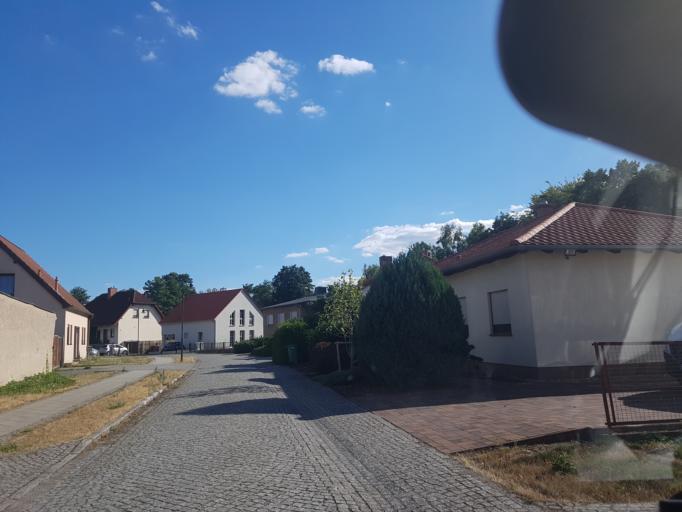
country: DE
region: Brandenburg
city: Juterbog
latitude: 52.0217
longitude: 13.1009
